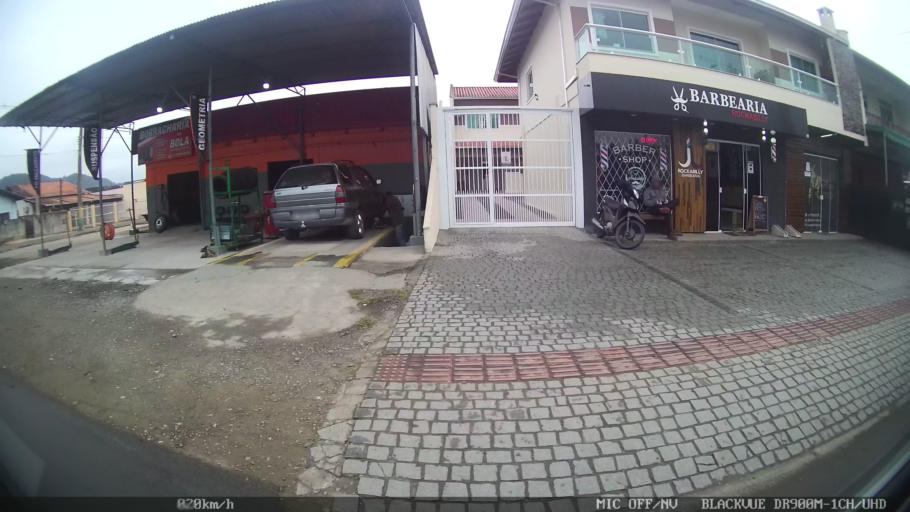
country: BR
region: Santa Catarina
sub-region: Joinville
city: Joinville
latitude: -26.2471
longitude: -48.8106
